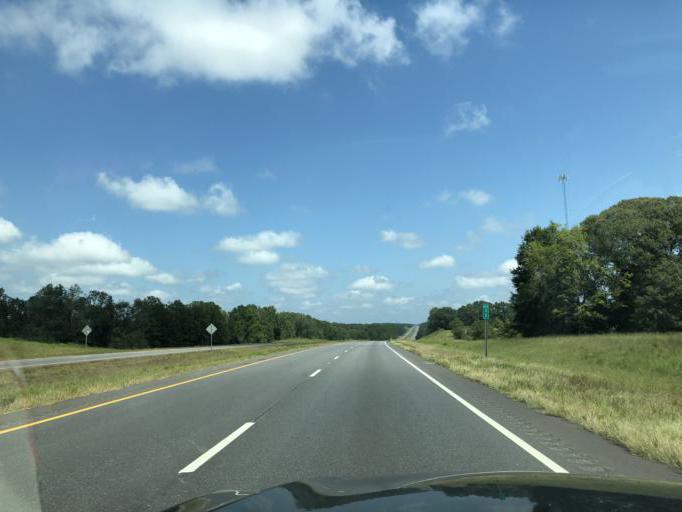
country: US
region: Alabama
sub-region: Henry County
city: Headland
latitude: 31.4562
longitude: -85.3091
